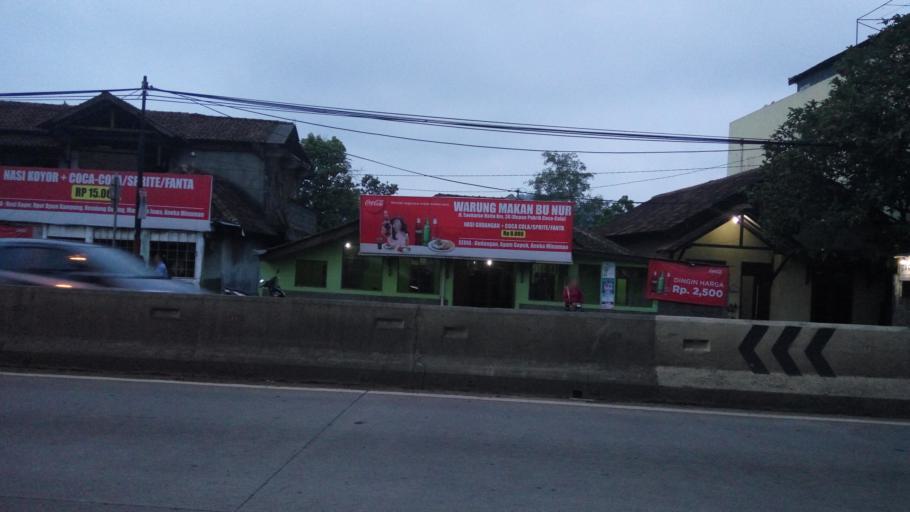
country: ID
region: Central Java
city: Ambarawa
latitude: -7.2113
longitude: 110.4246
